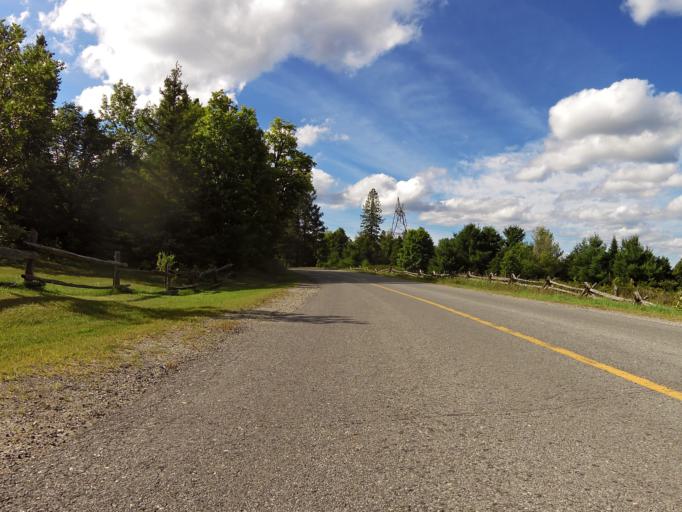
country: CA
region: Ontario
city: Renfrew
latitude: 45.0668
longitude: -76.6355
